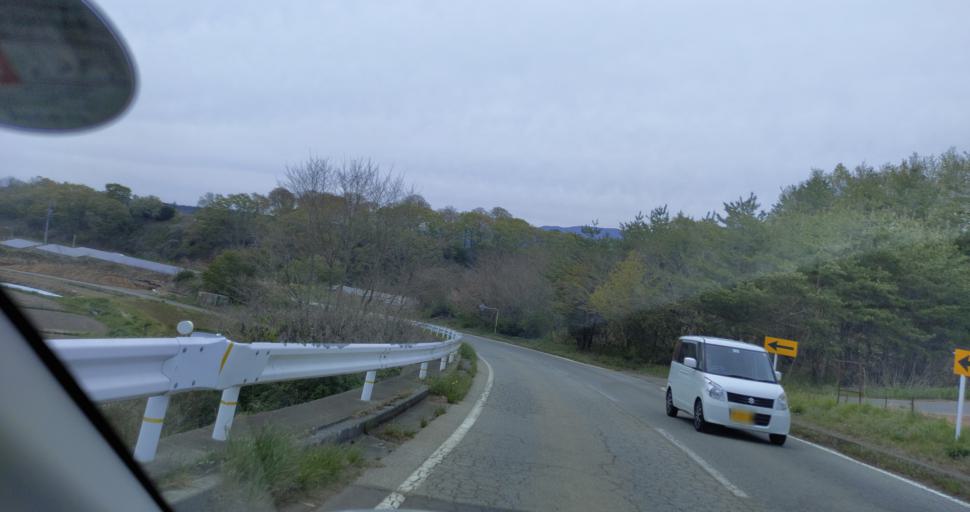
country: JP
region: Nagano
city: Komoro
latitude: 36.3242
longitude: 138.4926
